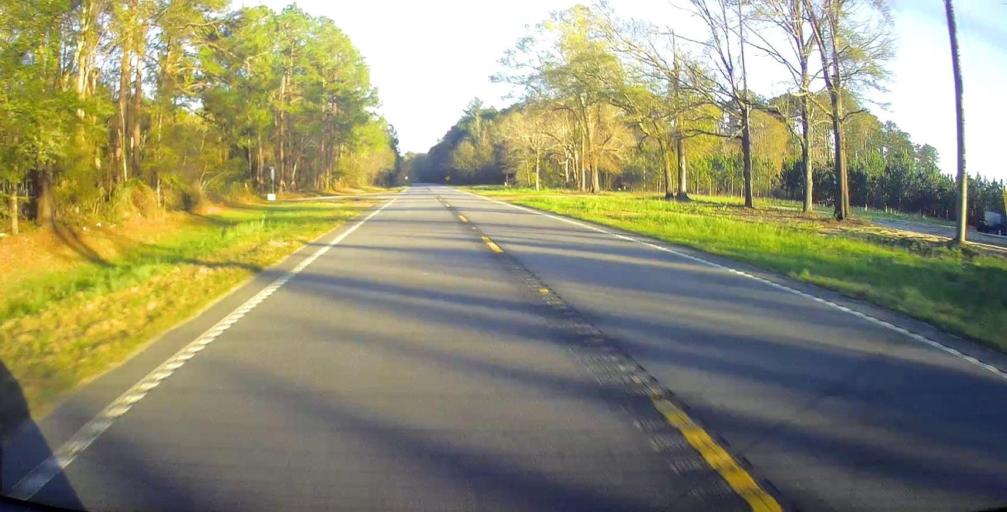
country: US
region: Georgia
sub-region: Wilcox County
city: Rochelle
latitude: 31.9545
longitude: -83.5778
